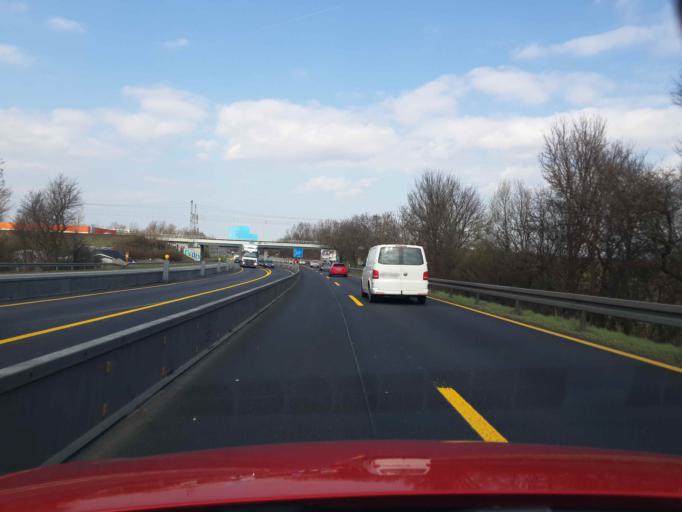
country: DE
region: Hesse
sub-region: Regierungsbezirk Darmstadt
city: Gross-Gerau
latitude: 49.9238
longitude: 8.5040
